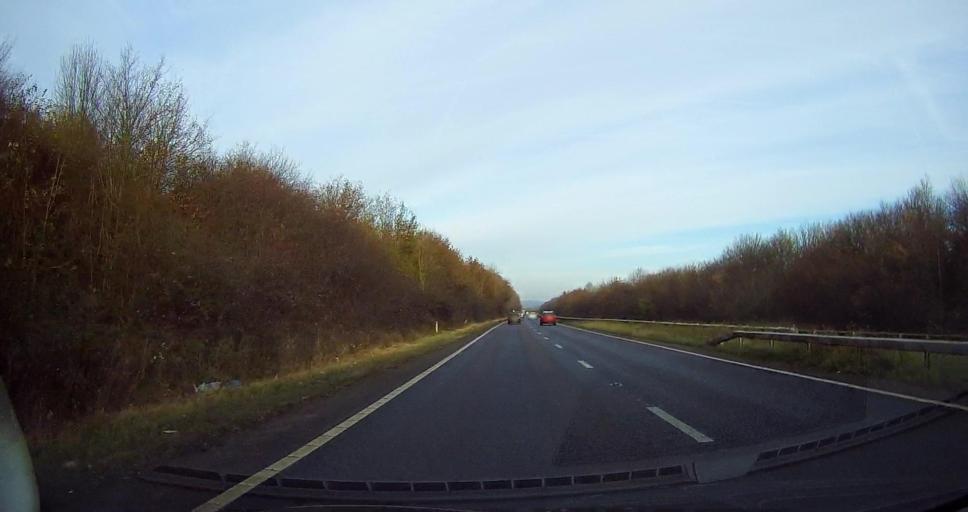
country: GB
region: England
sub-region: West Sussex
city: Hurstpierpoint
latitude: 50.9397
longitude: -0.1952
